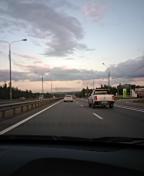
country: RU
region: Moskovskaya
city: Zhukovskiy
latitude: 55.5379
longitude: 38.0930
